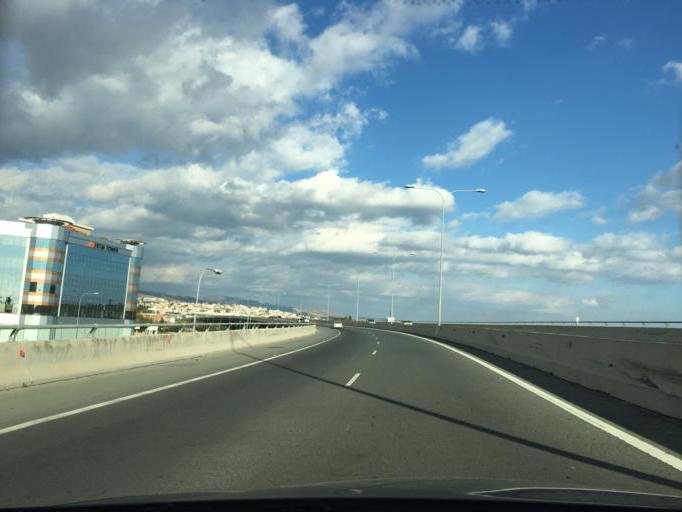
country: CY
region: Limassol
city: Pano Polemidia
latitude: 34.6889
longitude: 33.0078
